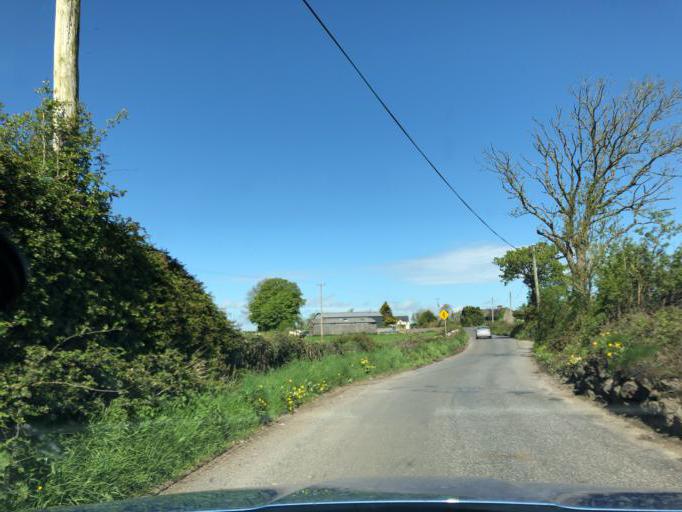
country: IE
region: Connaught
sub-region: County Galway
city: Portumna
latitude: 53.1556
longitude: -8.3860
